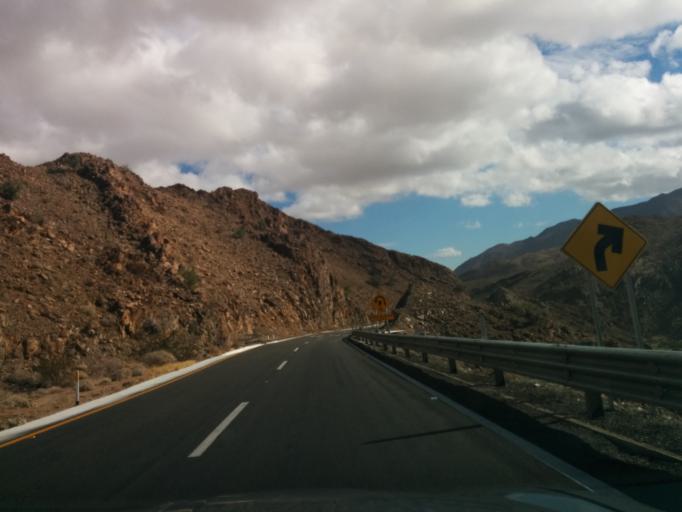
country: MX
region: Baja California
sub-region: Tecate
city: Cereso del Hongo
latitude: 32.5601
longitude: -115.9646
